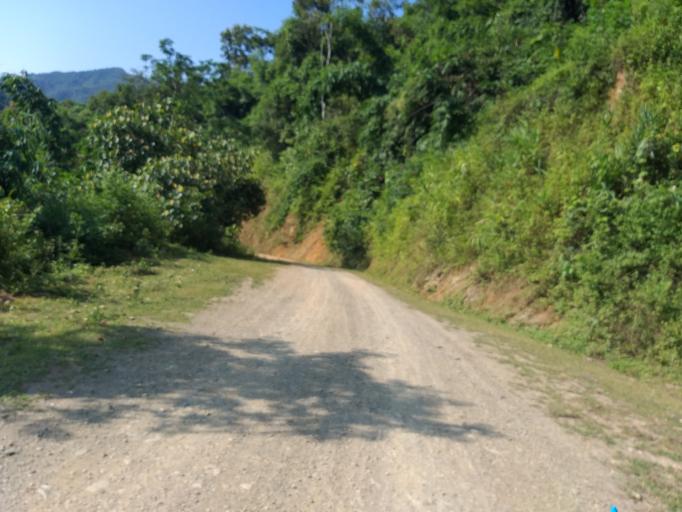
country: LA
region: Phongsali
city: Khoa
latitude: 21.1979
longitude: 102.6647
